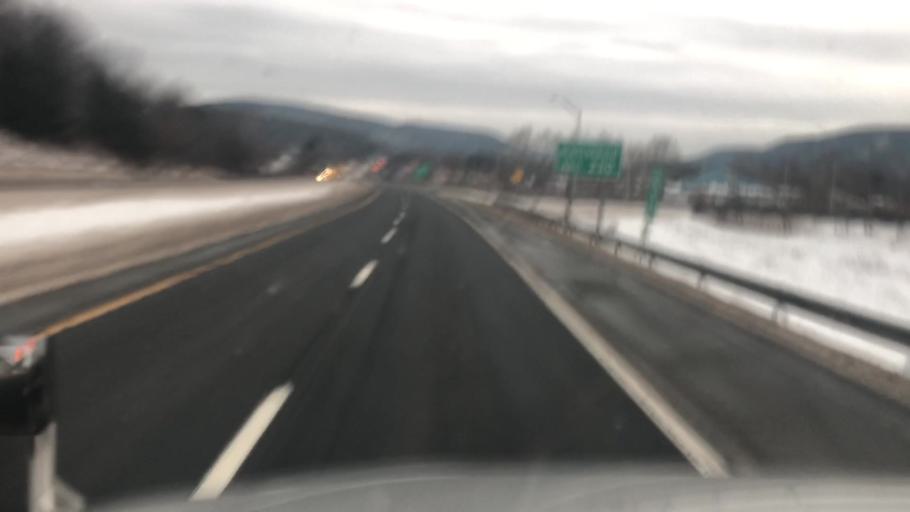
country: US
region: Pennsylvania
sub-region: Susquehanna County
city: Hallstead
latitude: 41.9860
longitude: -75.7485
